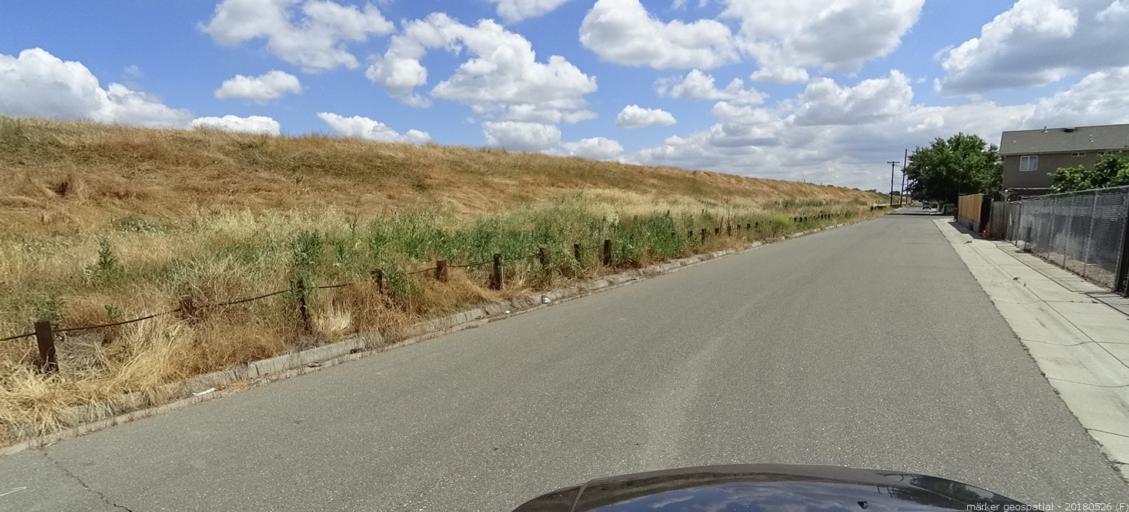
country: US
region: California
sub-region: Sacramento County
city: Sacramento
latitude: 38.6245
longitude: -121.4706
